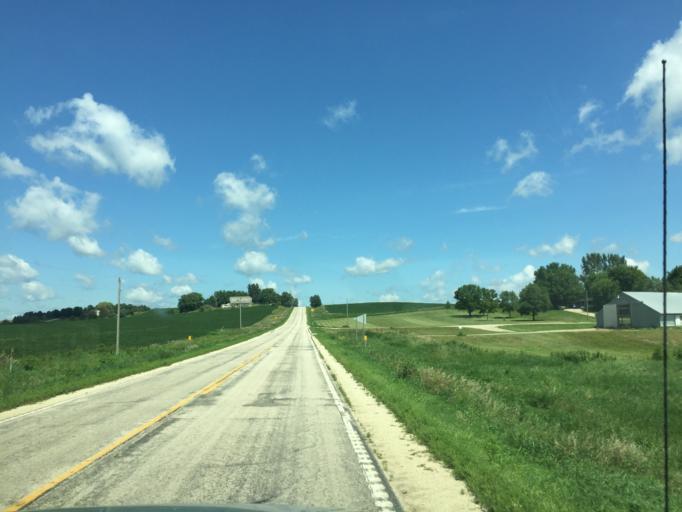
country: US
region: Minnesota
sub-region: Olmsted County
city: Byron
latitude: 44.0155
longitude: -92.6082
